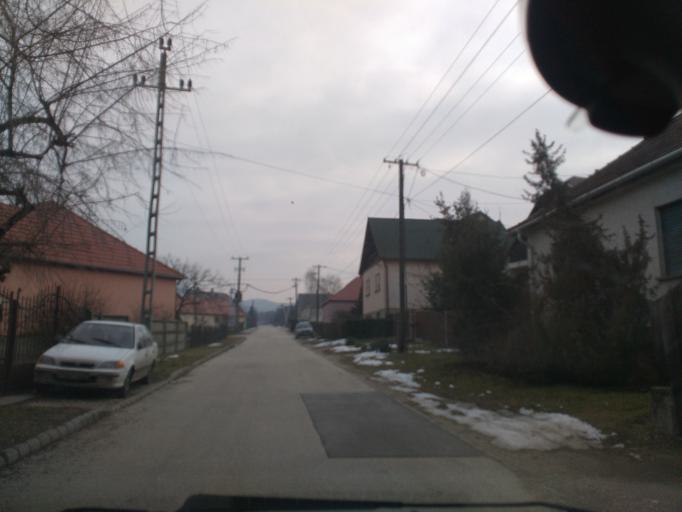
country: HU
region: Komarom-Esztergom
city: Piliscsev
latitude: 47.6717
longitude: 18.8119
